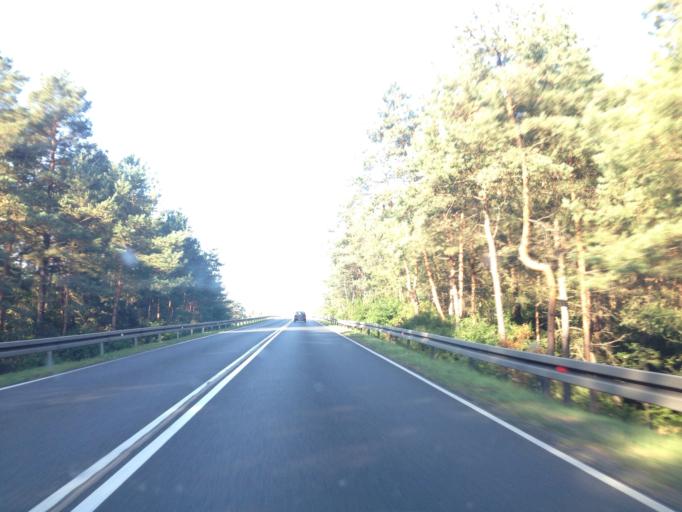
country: PL
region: Kujawsko-Pomorskie
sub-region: Powiat bydgoski
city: Nowa Wies Wielka
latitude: 53.0624
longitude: 18.0931
